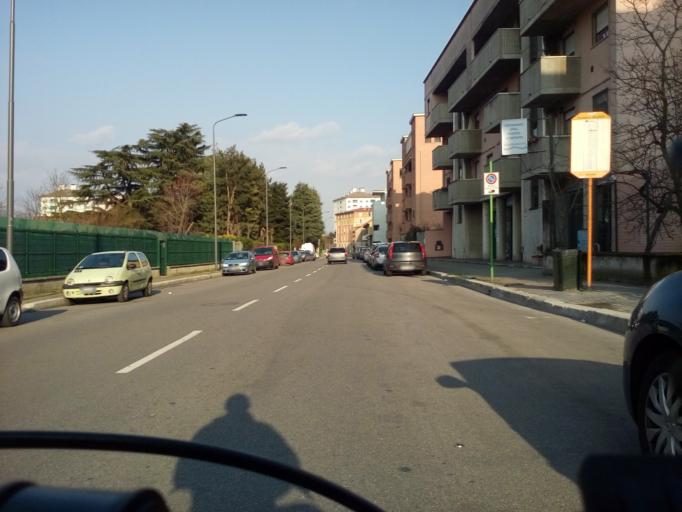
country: IT
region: Lombardy
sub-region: Citta metropolitana di Milano
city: Figino
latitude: 45.4690
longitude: 9.0870
